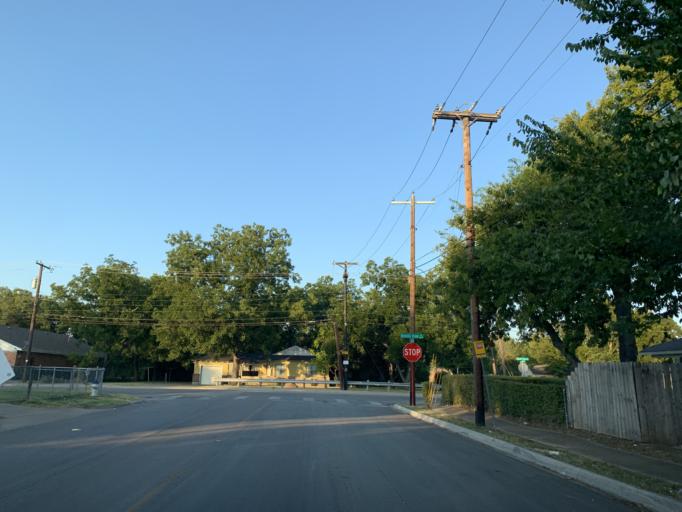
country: US
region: Texas
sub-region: Dallas County
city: Hutchins
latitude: 32.7040
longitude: -96.7724
